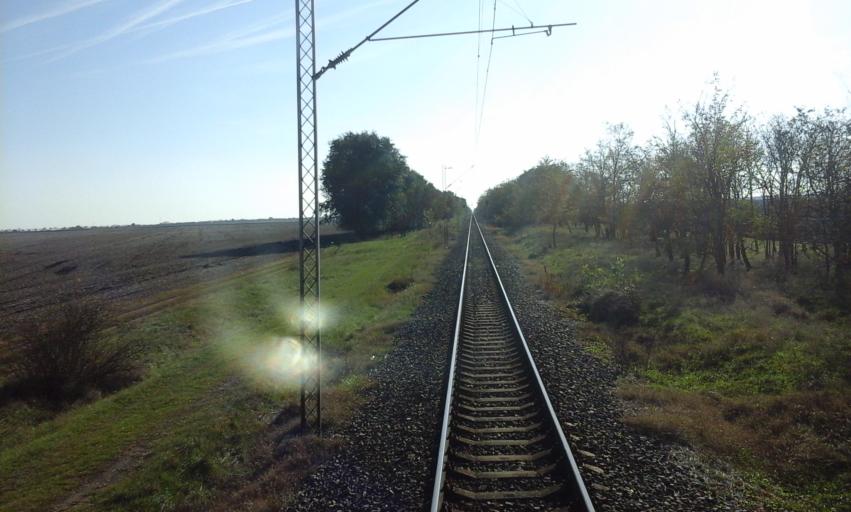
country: RS
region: Autonomna Pokrajina Vojvodina
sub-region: Severnobacki Okrug
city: Backa Topola
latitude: 45.8708
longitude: 19.6577
